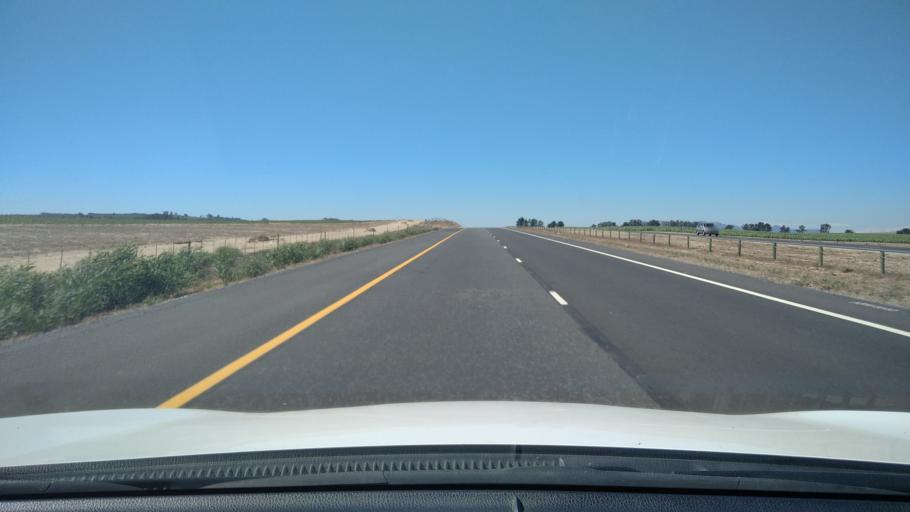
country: ZA
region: Western Cape
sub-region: West Coast District Municipality
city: Malmesbury
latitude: -33.5413
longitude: 18.6381
